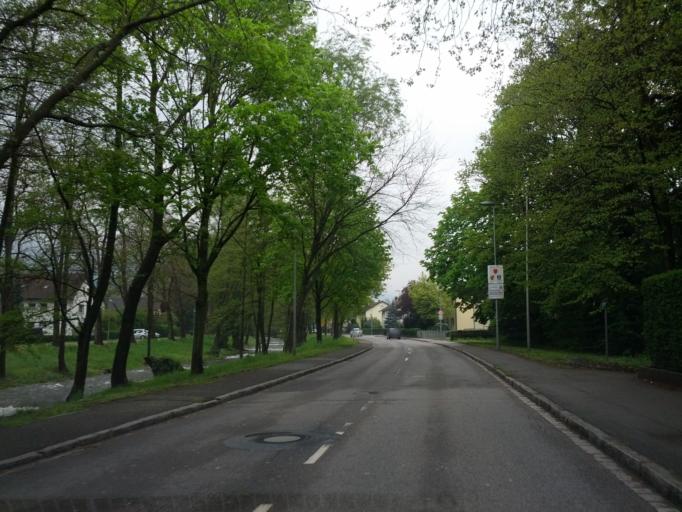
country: DE
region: Baden-Wuerttemberg
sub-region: Freiburg Region
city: Bad Krozingen
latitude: 47.8863
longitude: 7.7253
